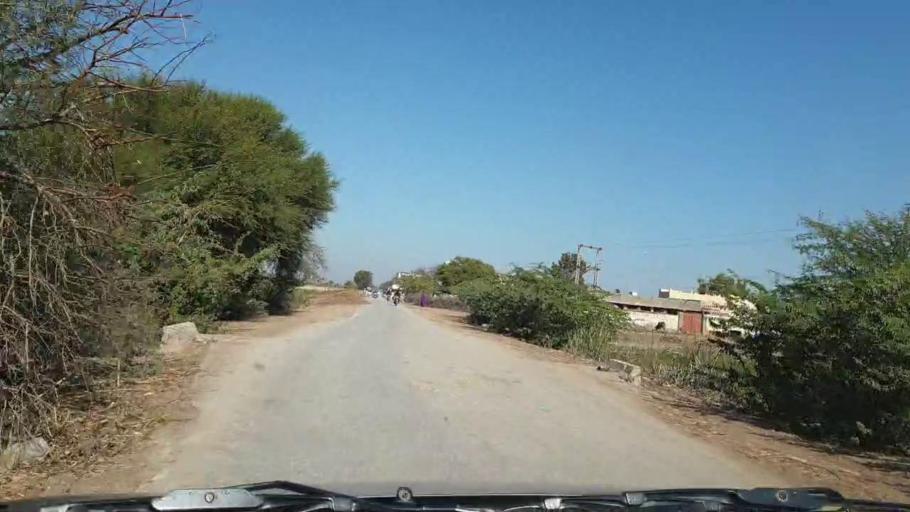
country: PK
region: Sindh
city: Sinjhoro
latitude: 26.1214
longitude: 68.8191
